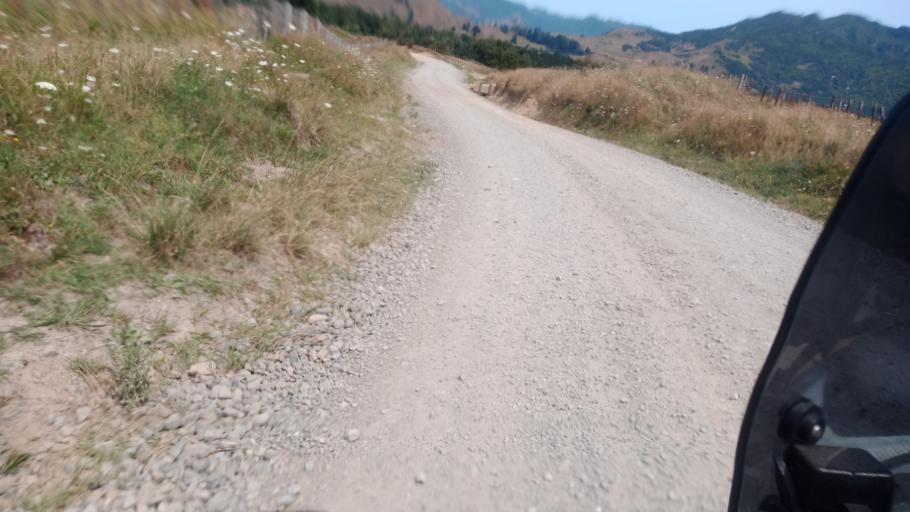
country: NZ
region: Bay of Plenty
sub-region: Opotiki District
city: Opotiki
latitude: -37.6554
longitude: 178.1191
